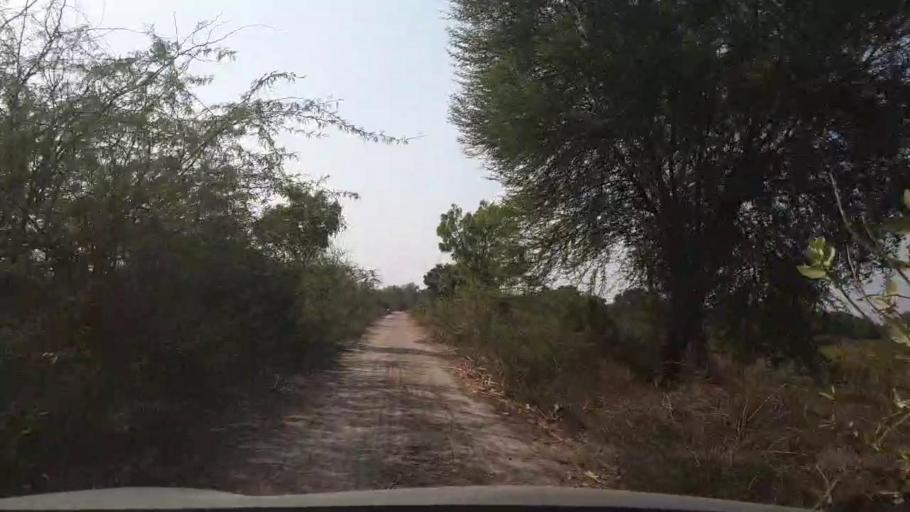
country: PK
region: Sindh
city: Tando Allahyar
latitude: 25.5933
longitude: 68.8142
